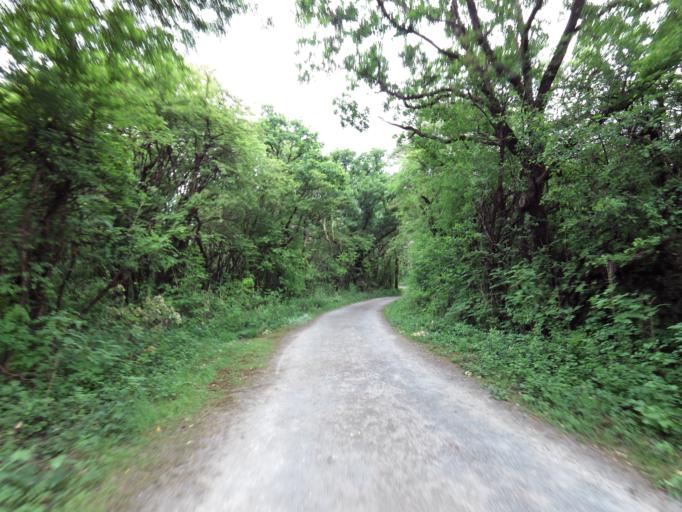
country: IE
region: Connaught
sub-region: County Galway
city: Gort
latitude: 53.0778
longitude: -8.8544
